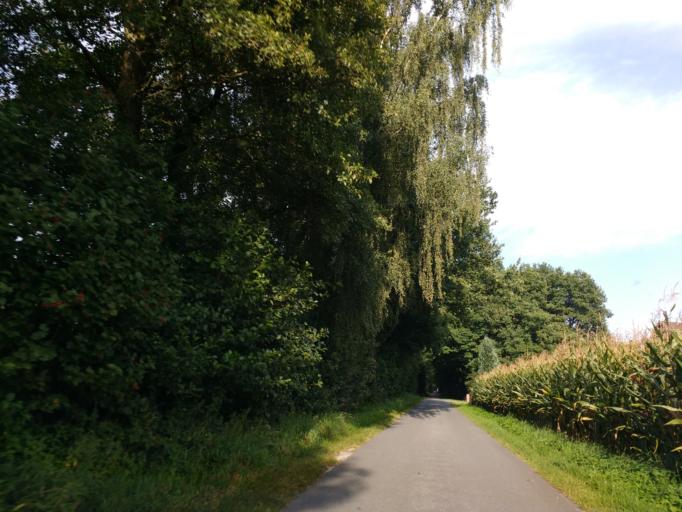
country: DE
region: North Rhine-Westphalia
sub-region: Regierungsbezirk Detmold
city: Hovelhof
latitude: 51.7780
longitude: 8.6241
